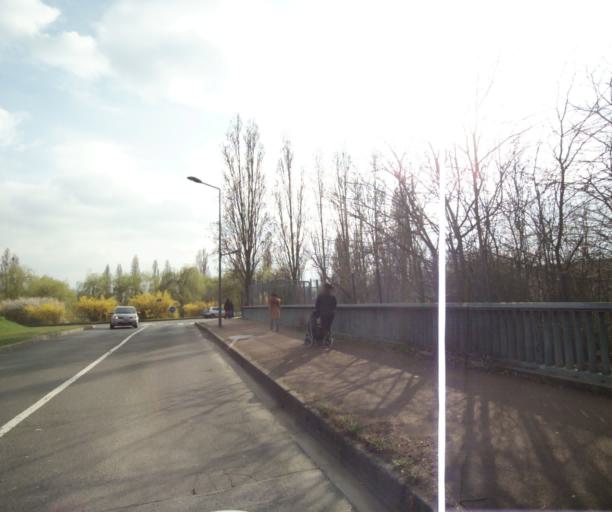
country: FR
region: Ile-de-France
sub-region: Departement du Val-d'Oise
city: Vaureal
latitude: 49.0488
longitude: 2.0447
